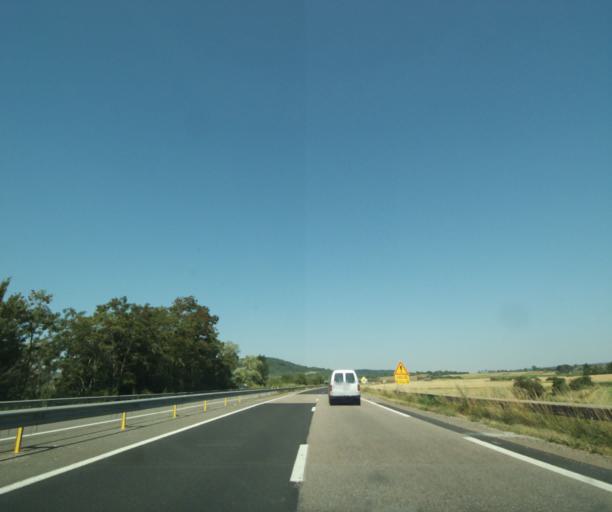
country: FR
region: Lorraine
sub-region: Departement de Meurthe-et-Moselle
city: Domgermain
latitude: 48.6454
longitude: 5.8538
